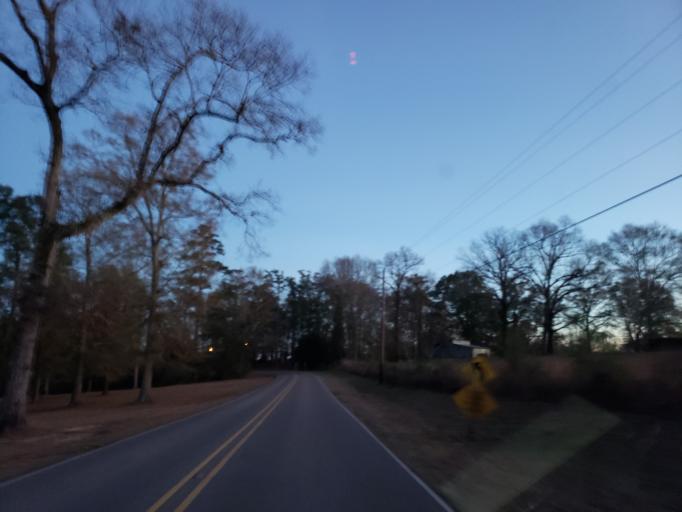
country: US
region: Mississippi
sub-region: Forrest County
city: Rawls Springs
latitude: 31.4258
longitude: -89.3531
